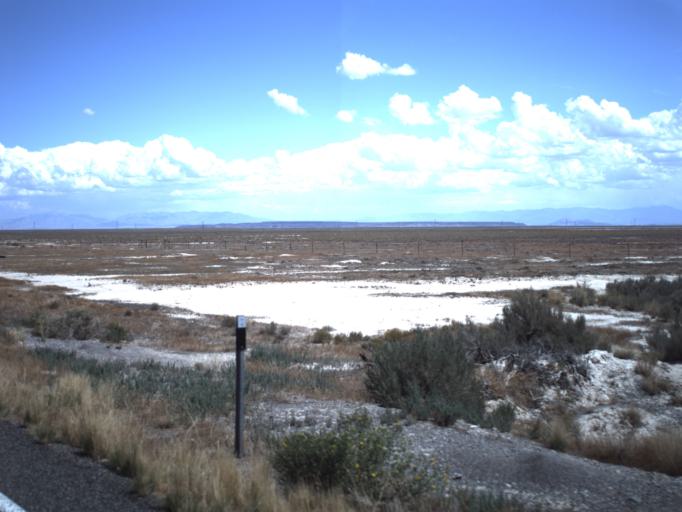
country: US
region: Utah
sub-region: Millard County
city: Delta
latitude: 39.2136
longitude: -112.9605
